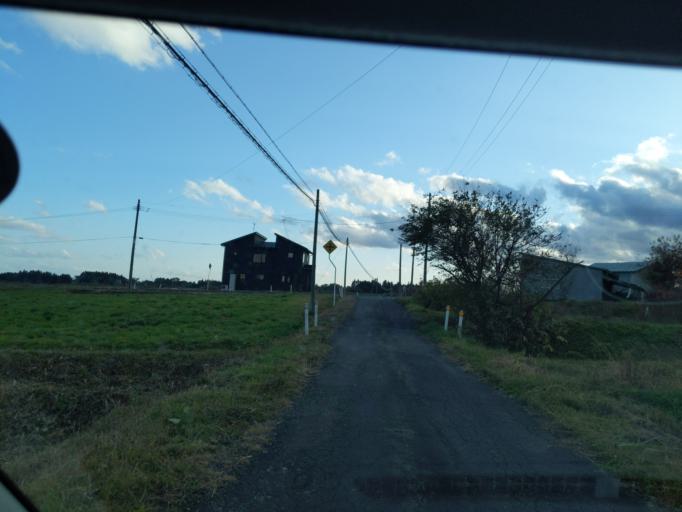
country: JP
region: Iwate
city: Mizusawa
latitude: 39.1023
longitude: 141.0395
